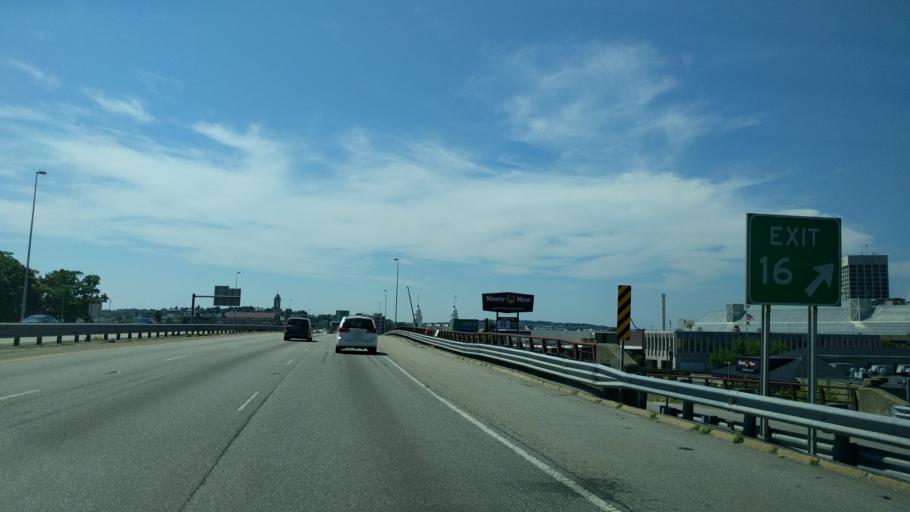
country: US
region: Massachusetts
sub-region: Worcester County
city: Worcester
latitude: 42.2676
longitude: -71.7934
